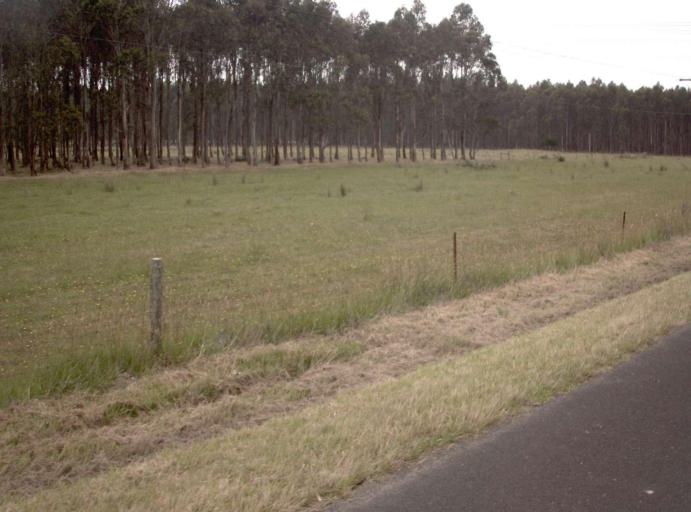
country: AU
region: Victoria
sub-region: Latrobe
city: Morwell
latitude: -38.2860
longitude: 146.4132
